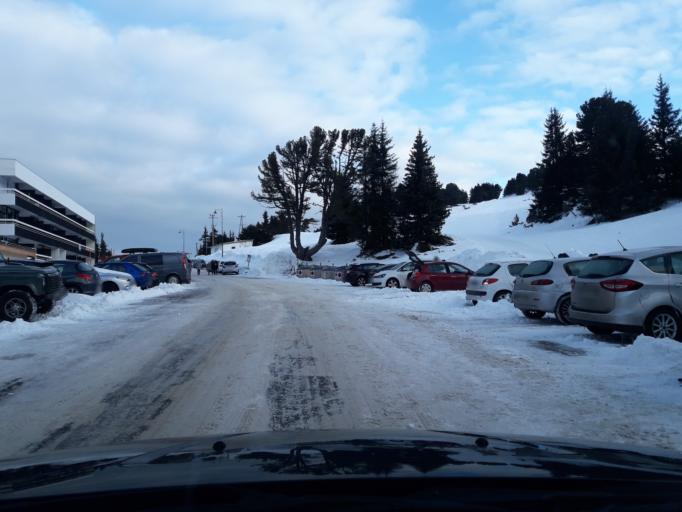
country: FR
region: Rhone-Alpes
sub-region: Departement de l'Isere
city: Livet-et-Gavet
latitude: 45.1135
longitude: 5.8787
